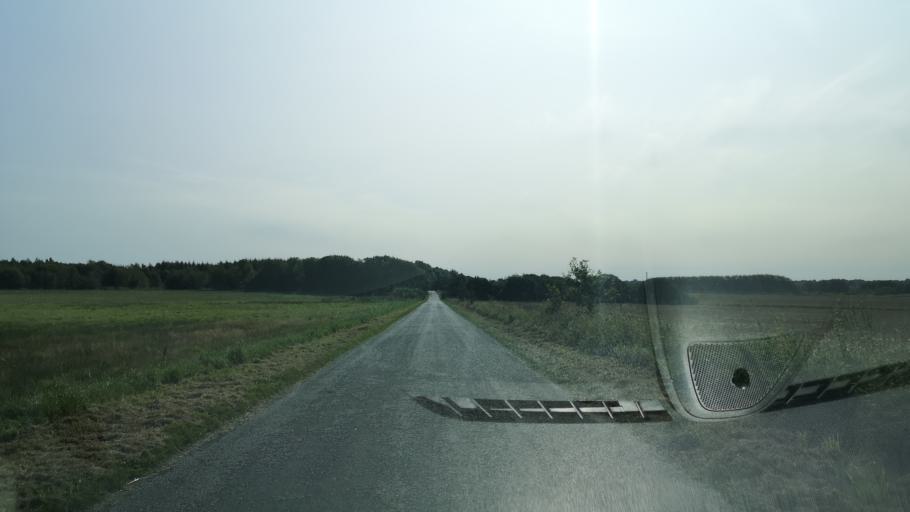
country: DK
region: Central Jutland
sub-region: Herning Kommune
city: Herning
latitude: 56.1734
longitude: 8.9540
